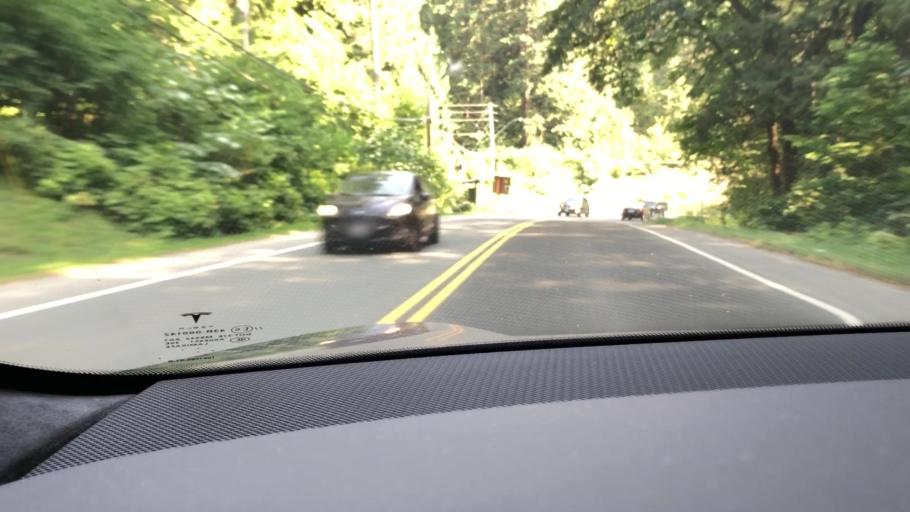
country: CA
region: British Columbia
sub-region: Fraser Valley Regional District
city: Chilliwack
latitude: 49.0804
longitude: -121.9796
